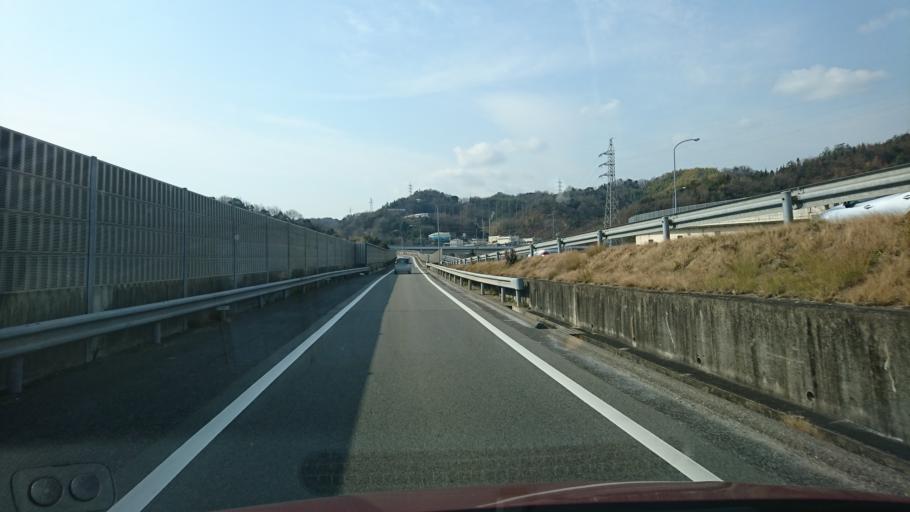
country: JP
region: Hiroshima
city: Onomichi
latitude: 34.4331
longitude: 133.2206
